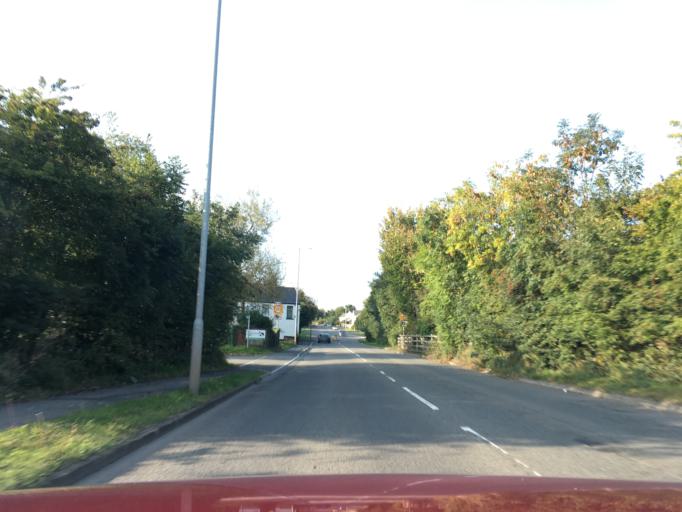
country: GB
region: Wales
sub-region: Torfaen County Borough
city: New Inn
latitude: 51.6740
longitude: -3.0193
